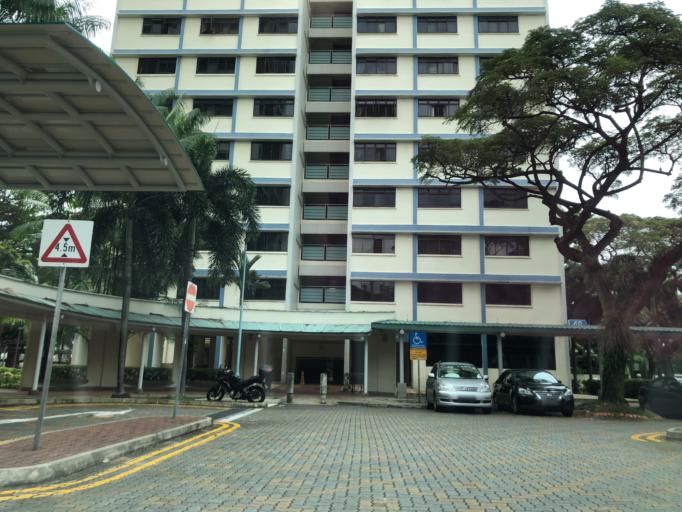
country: SG
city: Singapore
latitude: 1.3146
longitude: 103.8507
